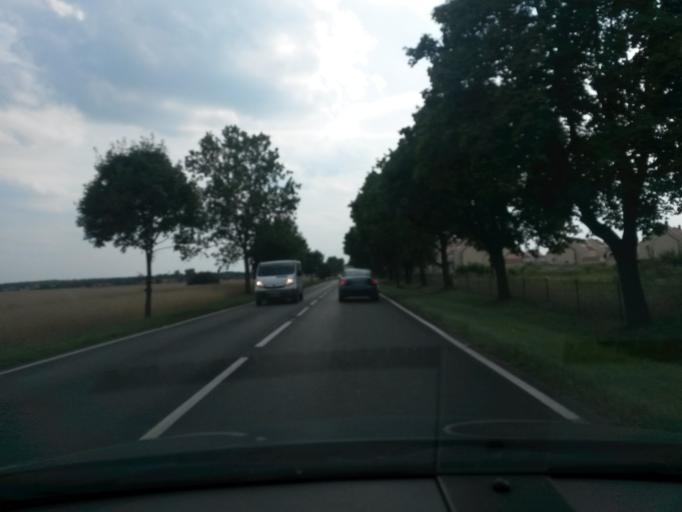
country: PL
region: Greater Poland Voivodeship
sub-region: Powiat poznanski
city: Kornik
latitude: 52.1887
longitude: 17.0578
